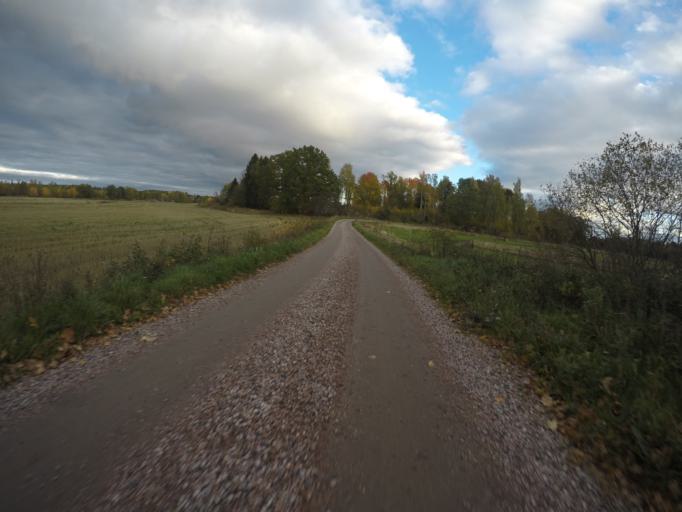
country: SE
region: Vaestmanland
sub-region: Arboga Kommun
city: Tyringe
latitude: 59.3012
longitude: 16.0041
